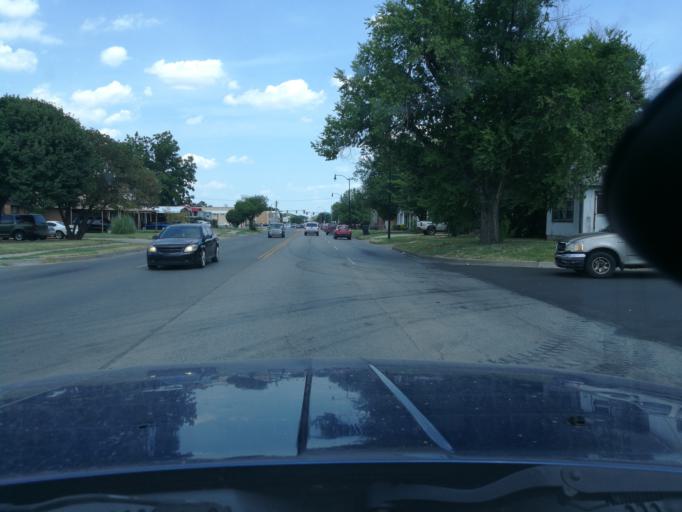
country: US
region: Oklahoma
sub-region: Oklahoma County
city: Oklahoma City
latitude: 35.4207
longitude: -97.5237
